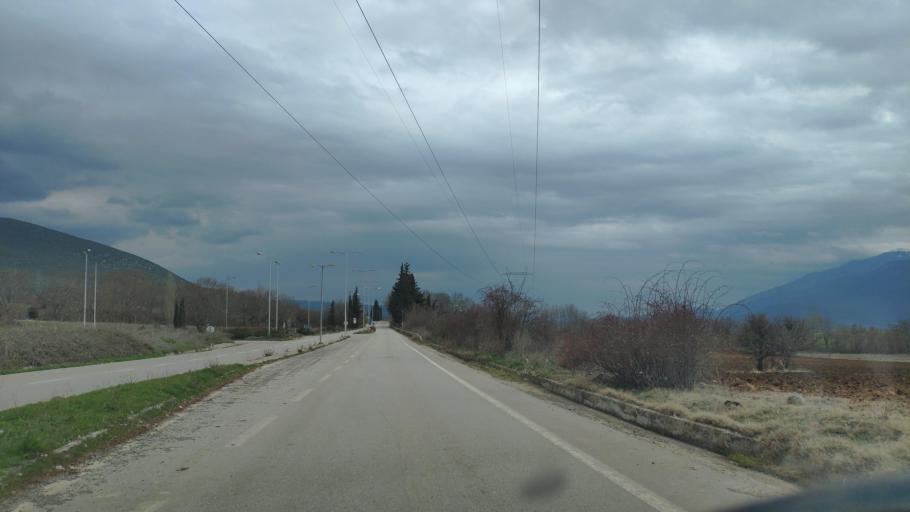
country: GR
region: Central Greece
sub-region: Nomos Fthiotidos
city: Amfikleia
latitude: 38.7089
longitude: 22.4883
